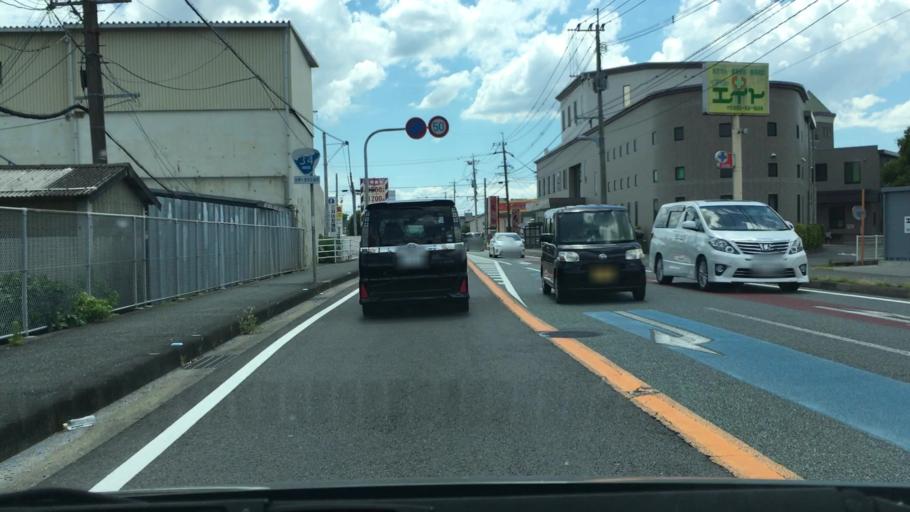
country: JP
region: Saga Prefecture
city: Kanzakimachi-kanzaki
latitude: 33.3316
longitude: 130.4132
